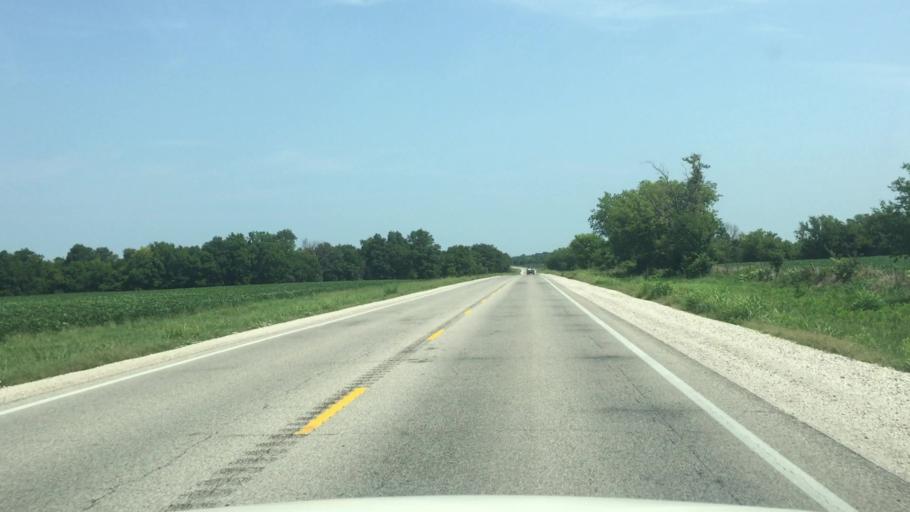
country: US
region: Kansas
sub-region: Montgomery County
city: Coffeyville
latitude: 37.1266
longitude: -95.5803
